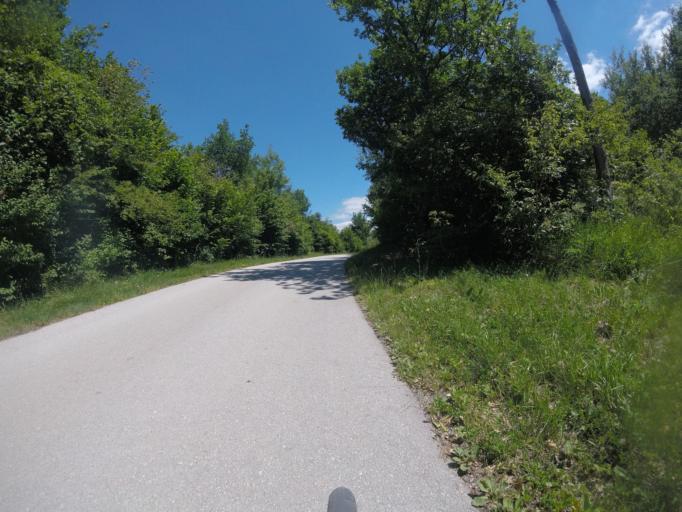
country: SI
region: Metlika
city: Metlika
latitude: 45.6939
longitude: 15.3925
